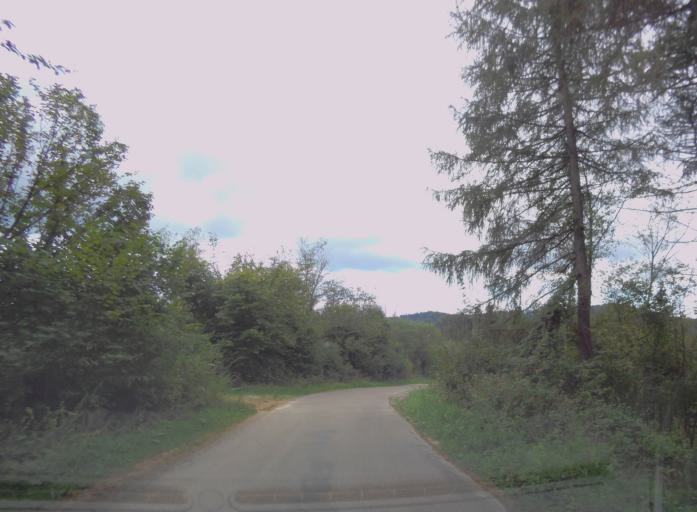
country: PL
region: Subcarpathian Voivodeship
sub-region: Powiat leski
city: Polanczyk
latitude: 49.2996
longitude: 22.5110
